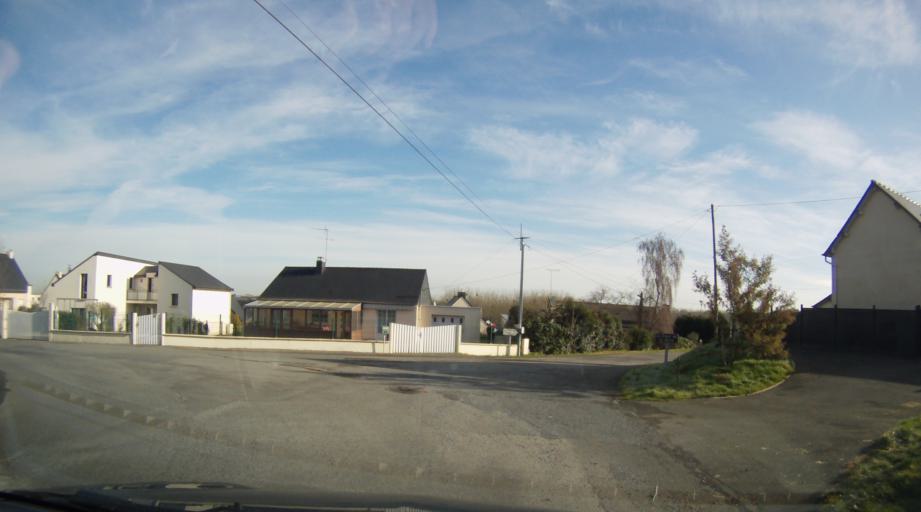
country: FR
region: Brittany
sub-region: Departement d'Ille-et-Vilaine
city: Bourgbarre
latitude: 47.9896
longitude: -1.6078
